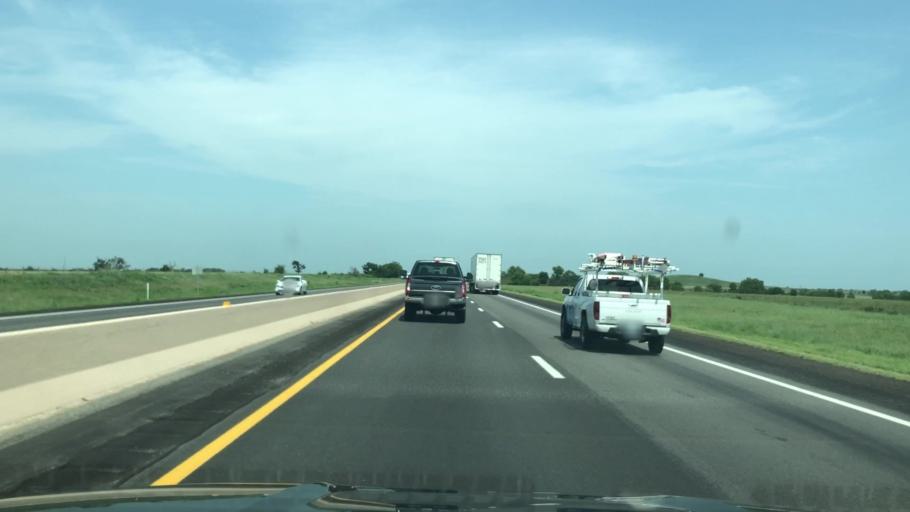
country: US
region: Oklahoma
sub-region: Ottawa County
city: Afton
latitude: 36.6807
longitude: -95.0422
